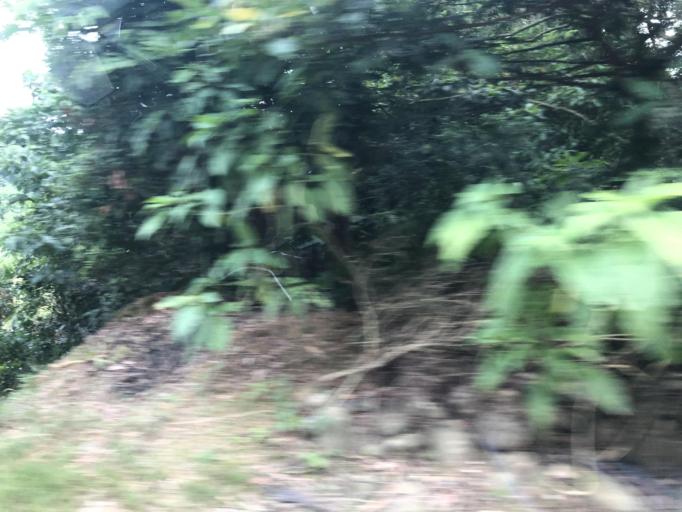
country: TW
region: Taiwan
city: Daxi
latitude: 24.9136
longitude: 121.3431
